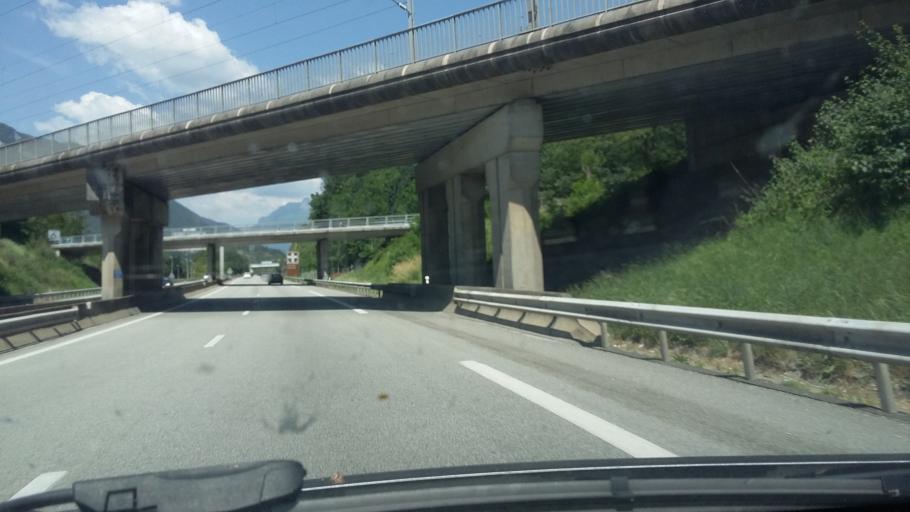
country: FR
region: Rhone-Alpes
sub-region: Departement de la Savoie
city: Montmelian
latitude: 45.4844
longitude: 6.0413
